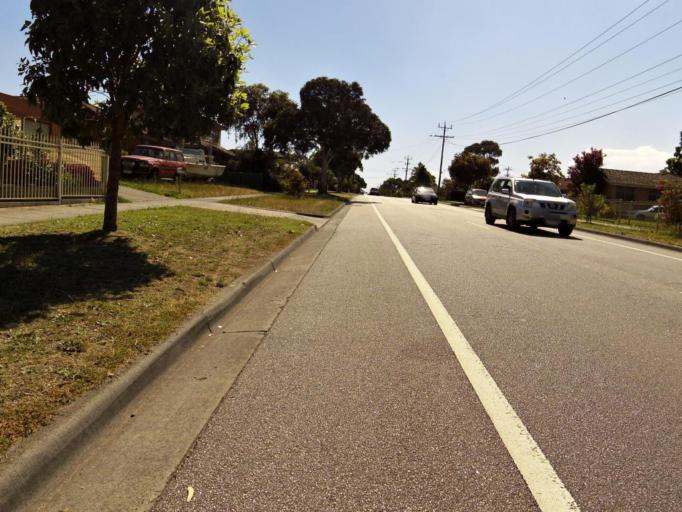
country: AU
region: Victoria
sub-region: Casey
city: Hampton Park
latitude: -38.0315
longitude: 145.2626
